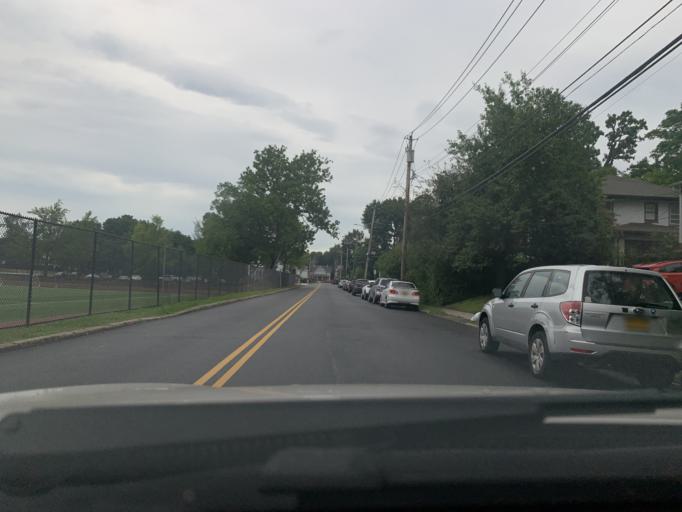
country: US
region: New York
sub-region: Westchester County
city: Ossining
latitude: 41.1590
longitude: -73.8570
